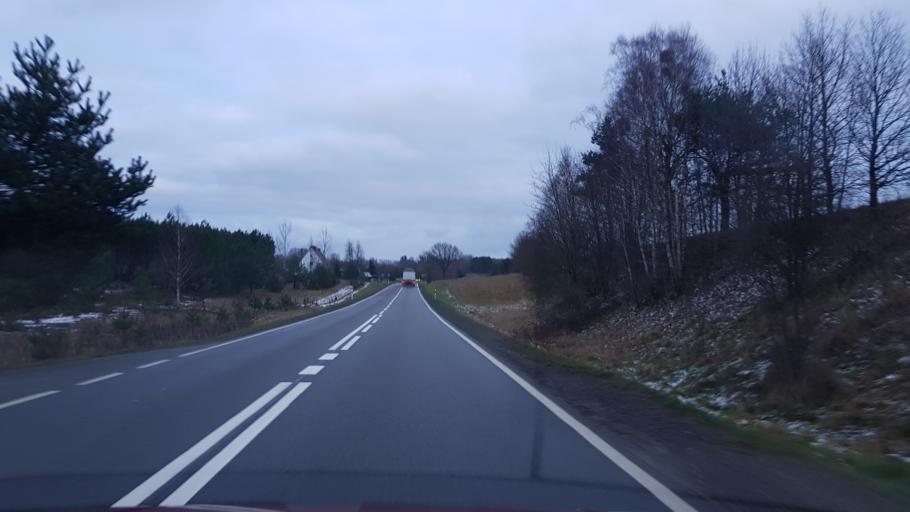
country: PL
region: Pomeranian Voivodeship
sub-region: Powiat bytowski
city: Tuchomie
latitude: 54.0394
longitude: 17.1972
